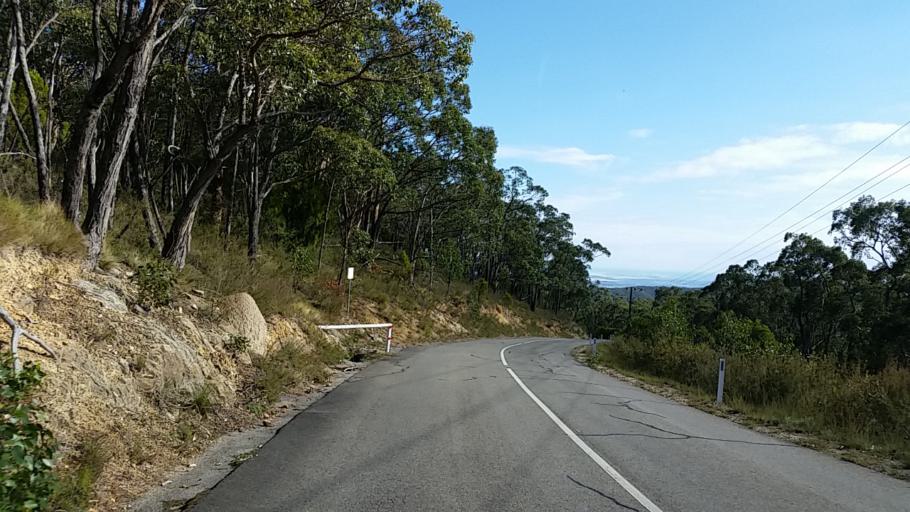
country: AU
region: South Australia
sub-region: Adelaide Hills
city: Crafers
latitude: -34.9699
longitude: 138.7033
